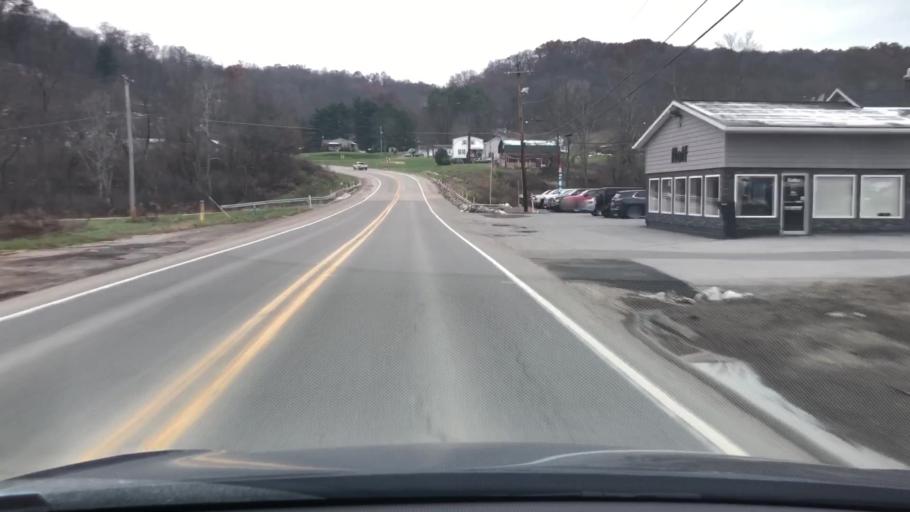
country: US
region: Pennsylvania
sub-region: Clarion County
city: Clarion
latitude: 41.0151
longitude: -79.2980
